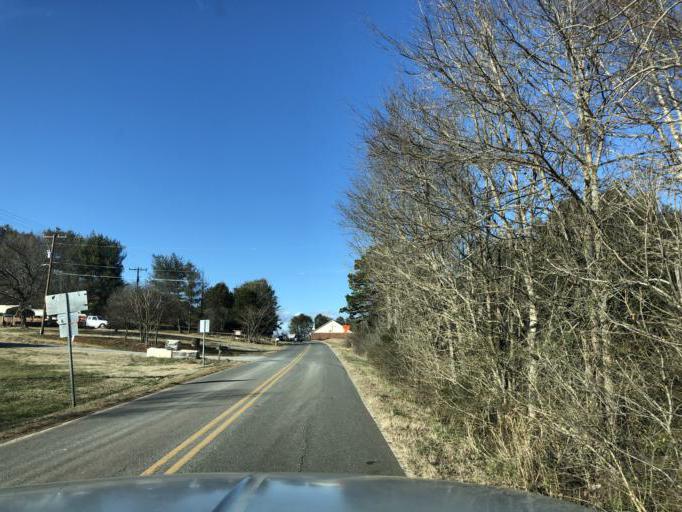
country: US
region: North Carolina
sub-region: Cleveland County
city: Shelby
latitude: 35.3360
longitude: -81.5397
